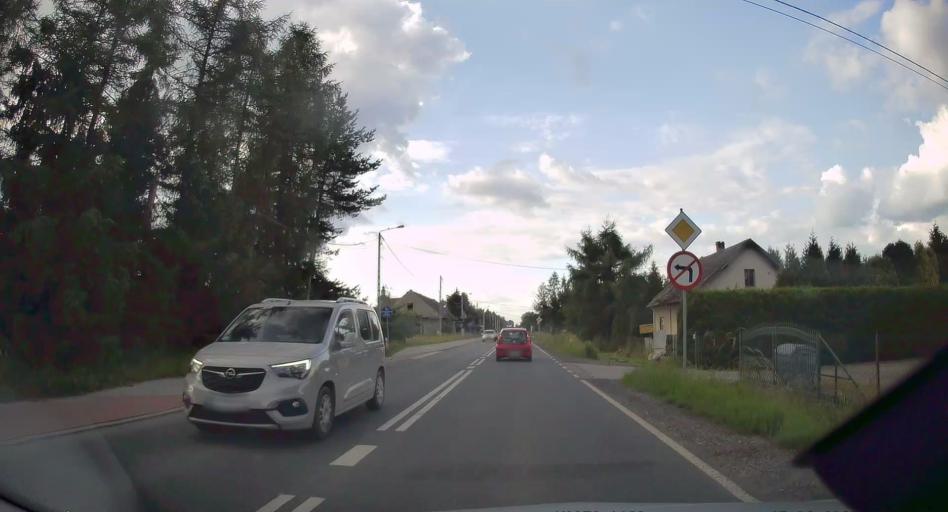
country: PL
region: Lesser Poland Voivodeship
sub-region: Powiat oswiecimski
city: Nowa Wies
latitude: 49.9001
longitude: 19.2178
